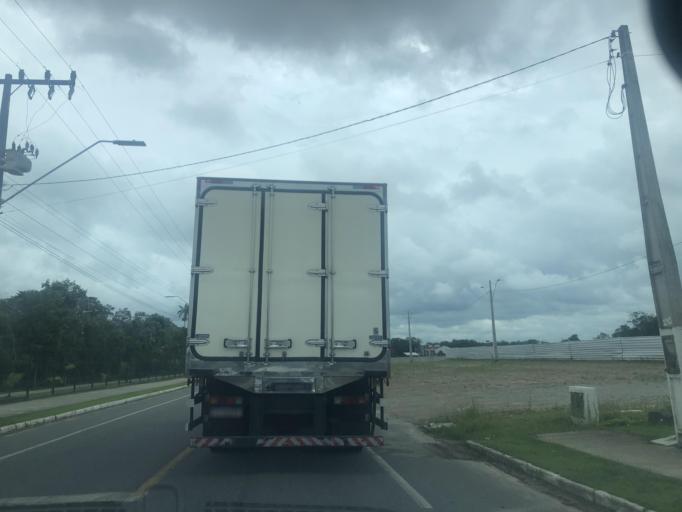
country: BR
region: Santa Catarina
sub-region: Joinville
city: Joinville
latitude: -26.3780
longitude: -48.7254
